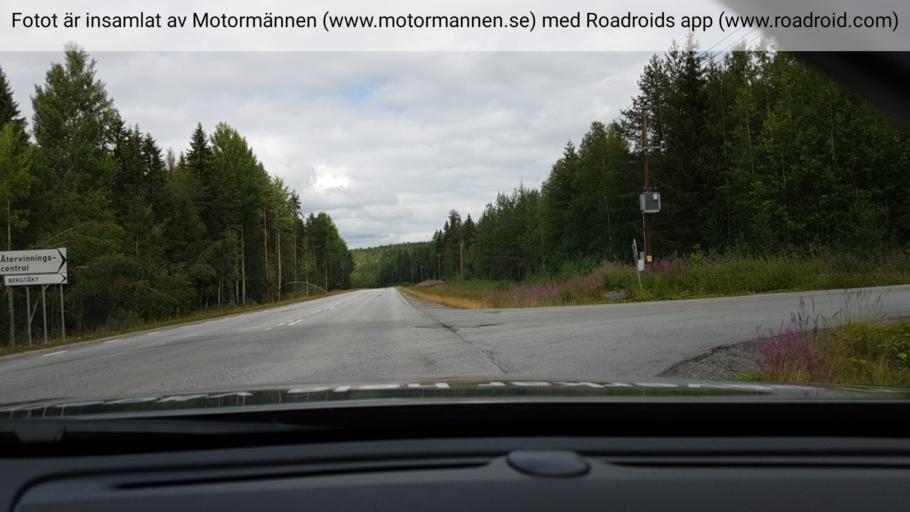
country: SE
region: Vaesterbotten
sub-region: Vannas Kommun
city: Vaennaes
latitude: 63.9354
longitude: 19.7712
